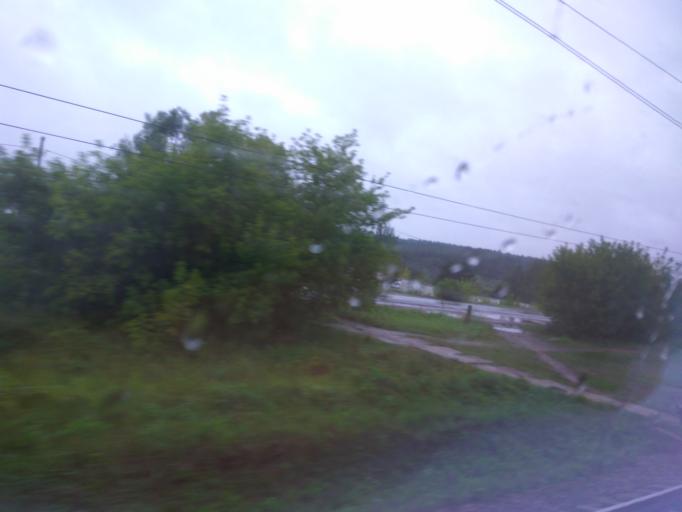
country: RU
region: Moskovskaya
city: Kashira
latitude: 54.8725
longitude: 38.1211
